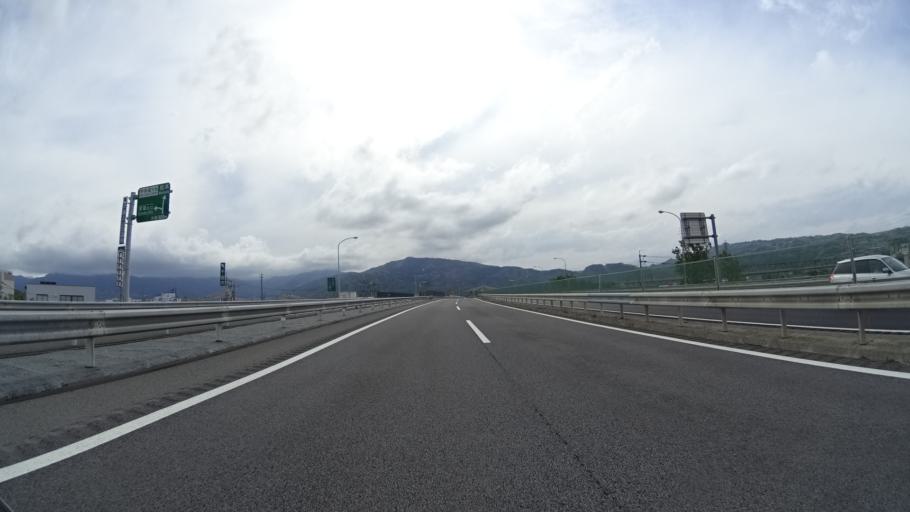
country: JP
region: Nagano
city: Nagano-shi
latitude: 36.5519
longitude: 138.1376
